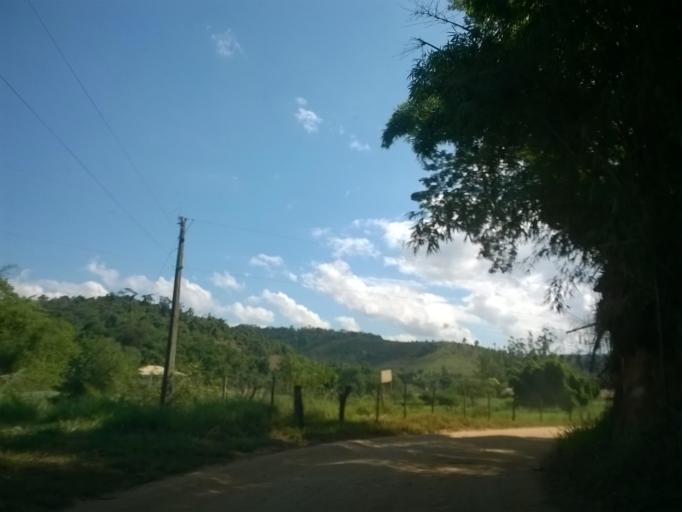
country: BR
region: Minas Gerais
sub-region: Uba
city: Uba
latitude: -21.0708
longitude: -42.9001
